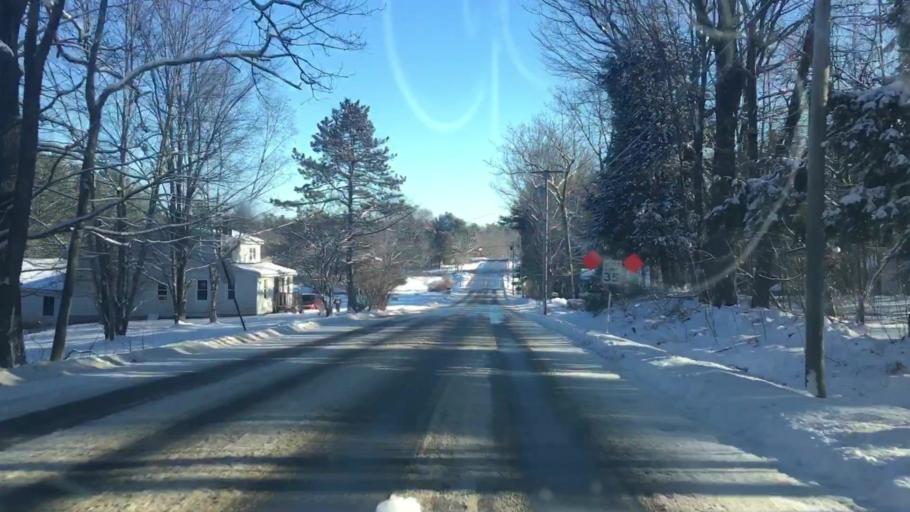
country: US
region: Maine
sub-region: Androscoggin County
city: Lisbon Falls
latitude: 43.9370
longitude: -70.0635
